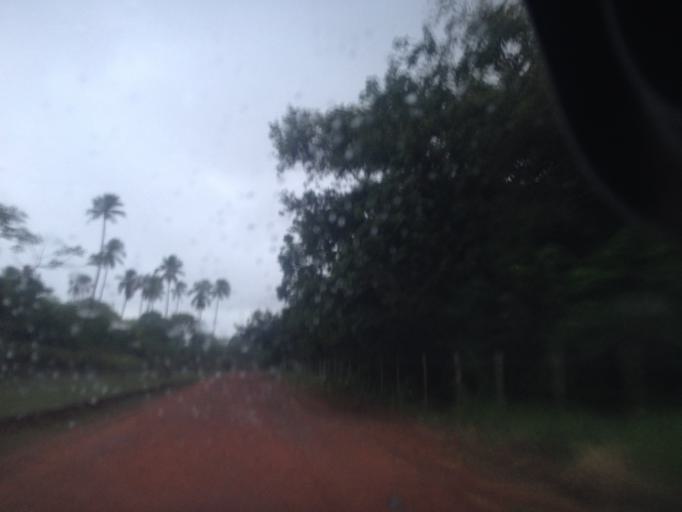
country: BR
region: Bahia
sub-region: Mata De Sao Joao
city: Mata de Sao Joao
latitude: -12.5787
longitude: -38.0316
